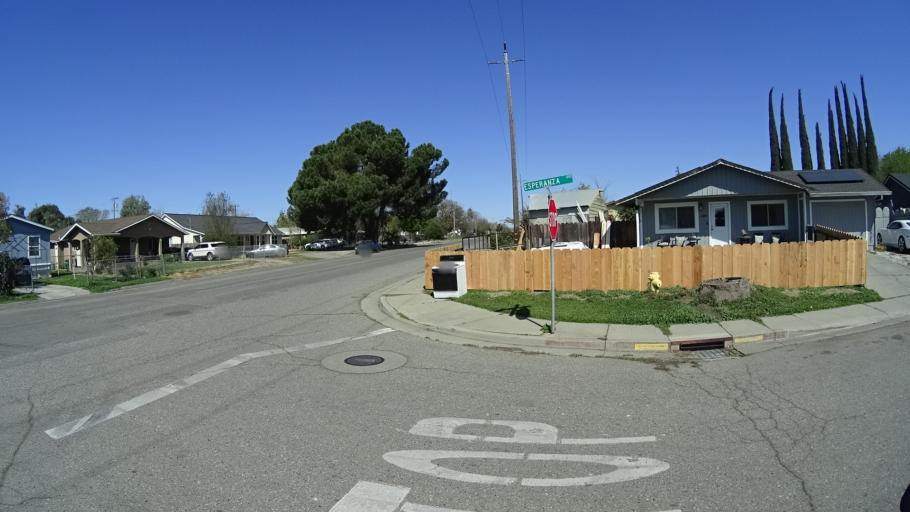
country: US
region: California
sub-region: Glenn County
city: Hamilton City
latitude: 39.7418
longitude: -122.0065
